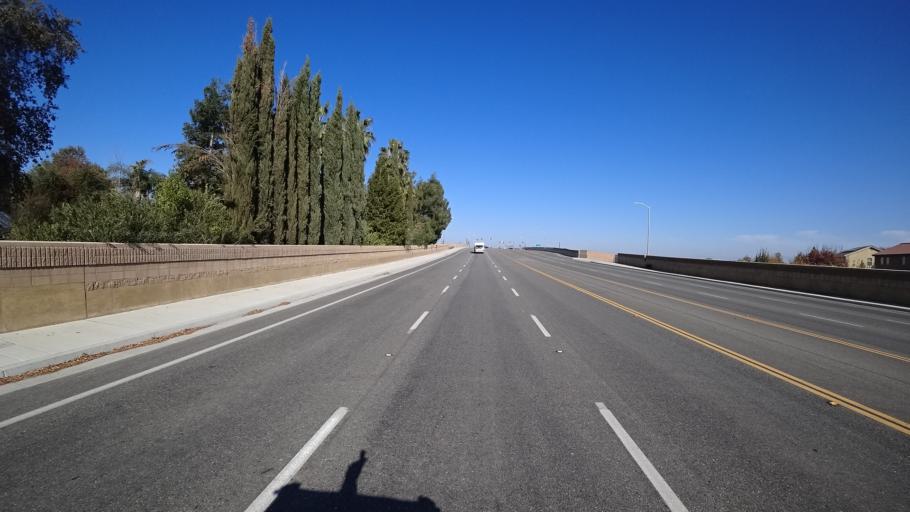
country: US
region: California
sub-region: Kern County
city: Rosedale
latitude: 35.3581
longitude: -119.1456
